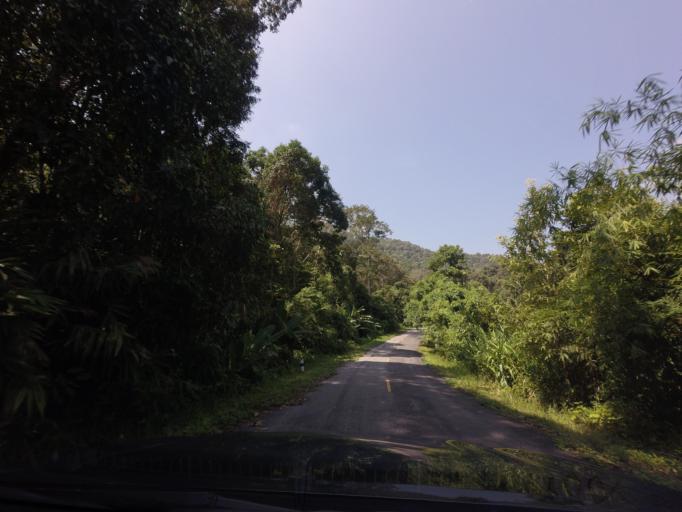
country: TH
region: Loei
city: Na Haeo
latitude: 17.5680
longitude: 100.9733
